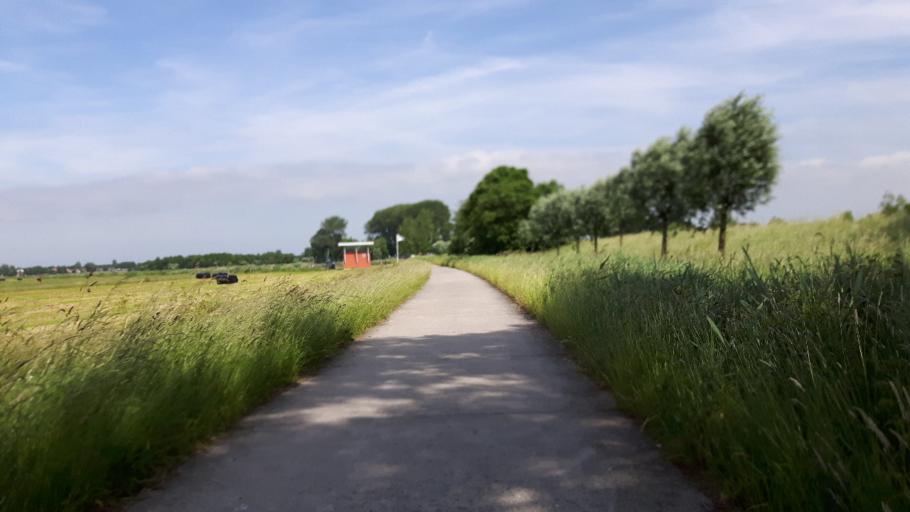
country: NL
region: North Holland
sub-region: Gemeente Uithoorn
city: Uithoorn
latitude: 52.2271
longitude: 4.7958
